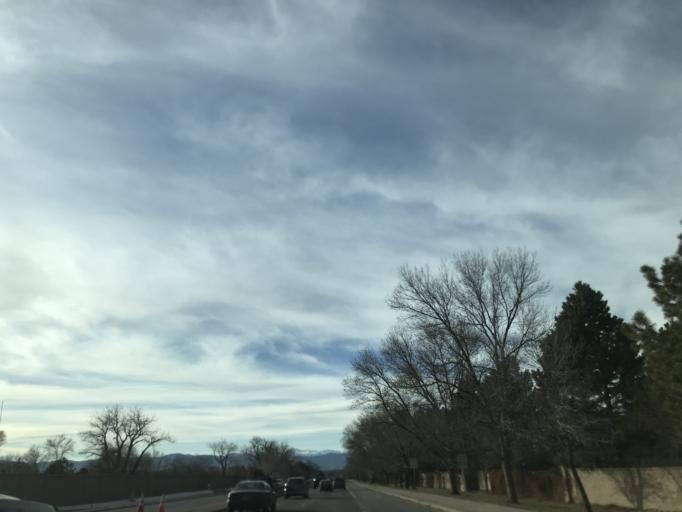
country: US
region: Colorado
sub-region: Arapahoe County
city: Greenwood Village
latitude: 39.6243
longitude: -104.9512
